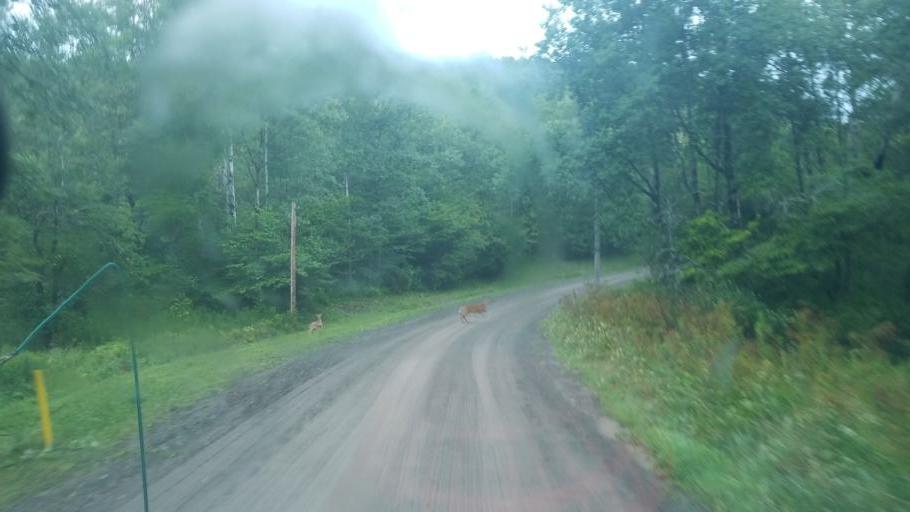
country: US
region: Pennsylvania
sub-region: Potter County
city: Galeton
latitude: 41.8429
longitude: -77.7964
